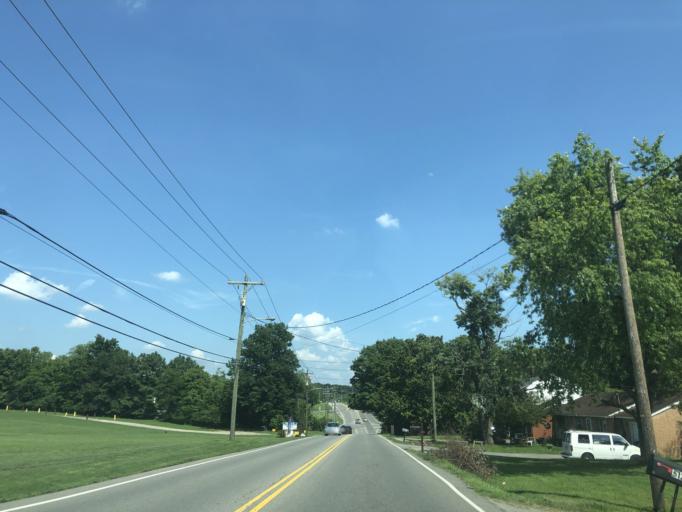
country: US
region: Tennessee
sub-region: Davidson County
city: Lakewood
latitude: 36.1581
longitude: -86.6386
